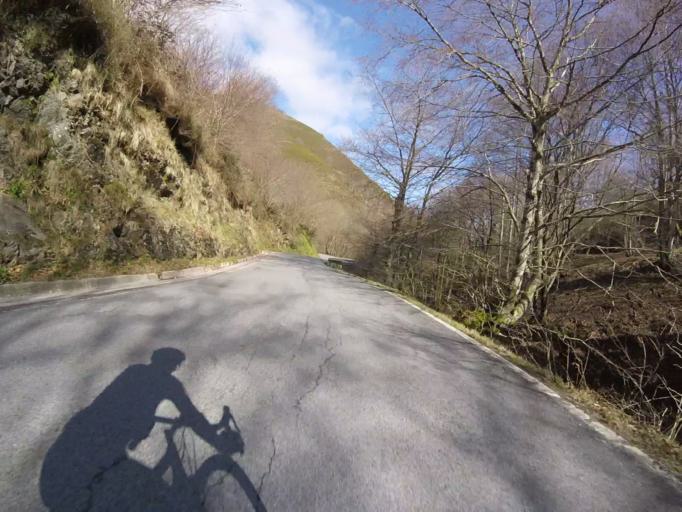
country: ES
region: Navarre
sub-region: Provincia de Navarra
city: Ezkurra
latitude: 43.0921
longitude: -1.8661
